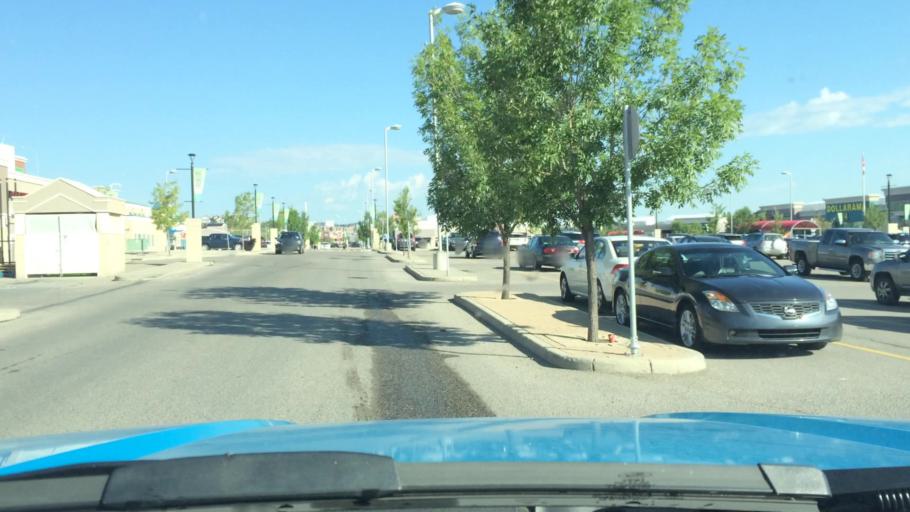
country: CA
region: Alberta
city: Calgary
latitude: 51.1605
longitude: -114.1230
